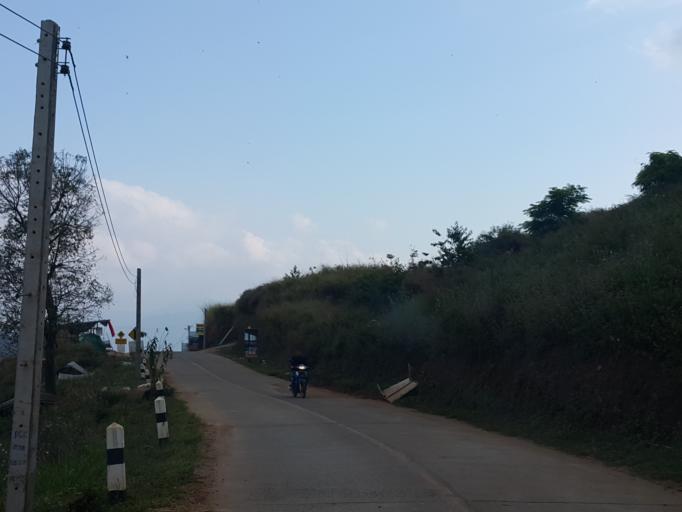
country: TH
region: Chiang Mai
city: Samoeng
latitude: 18.9316
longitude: 98.8166
